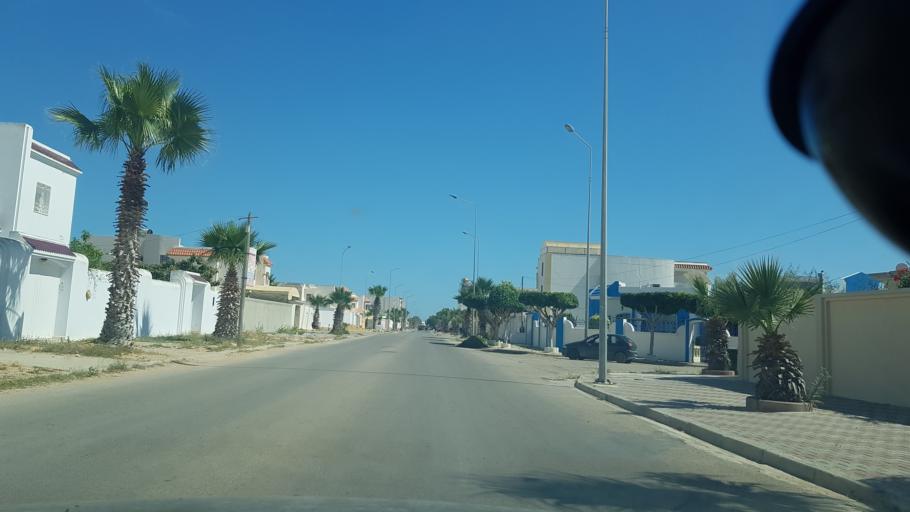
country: TN
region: Safaqis
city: Al Qarmadah
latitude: 34.8308
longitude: 10.7565
